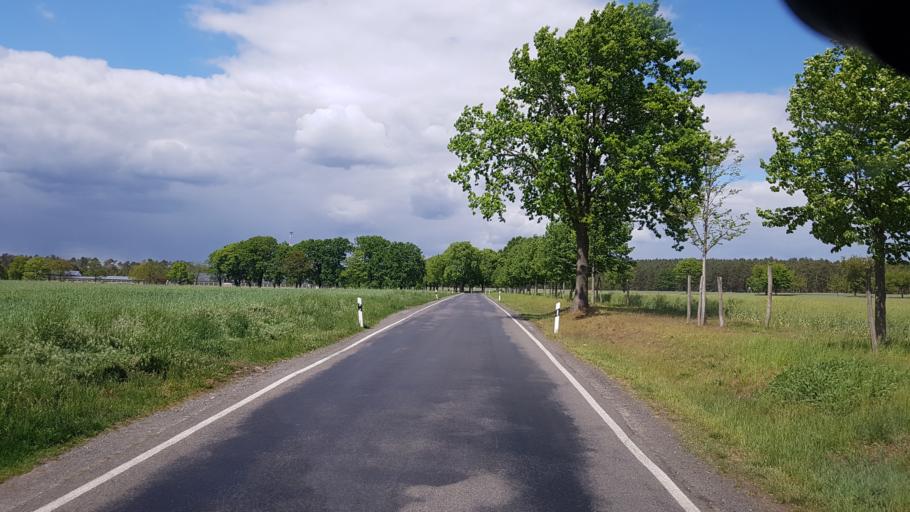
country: DE
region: Brandenburg
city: Bronkow
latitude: 51.6535
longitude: 13.9223
